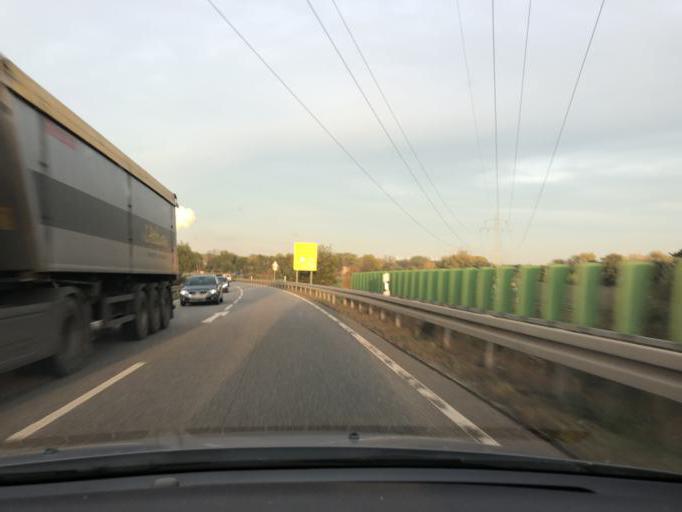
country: DE
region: Saxony-Anhalt
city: Zeitz
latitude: 51.0809
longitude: 12.1610
